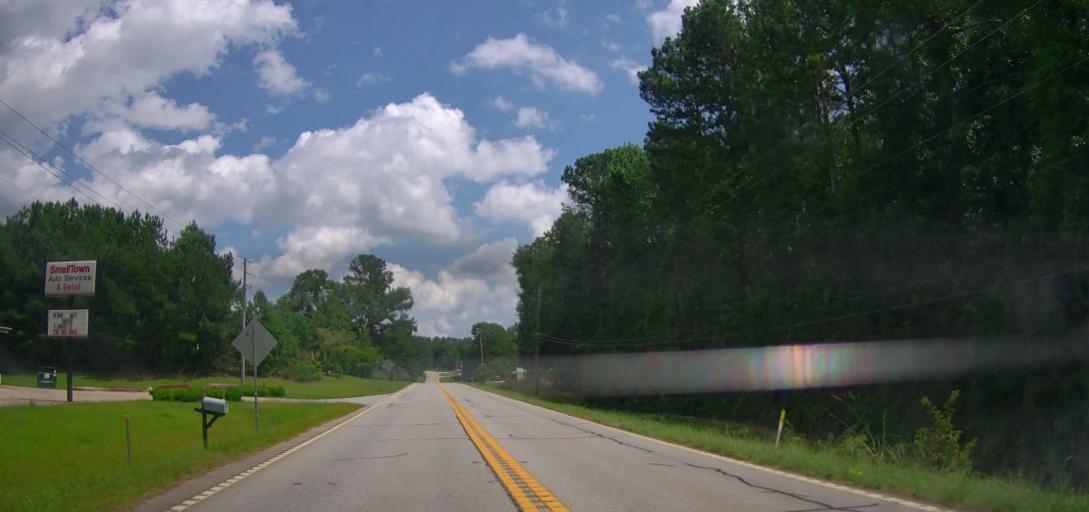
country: US
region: Georgia
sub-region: Heard County
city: Franklin
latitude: 33.2885
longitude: -85.1166
